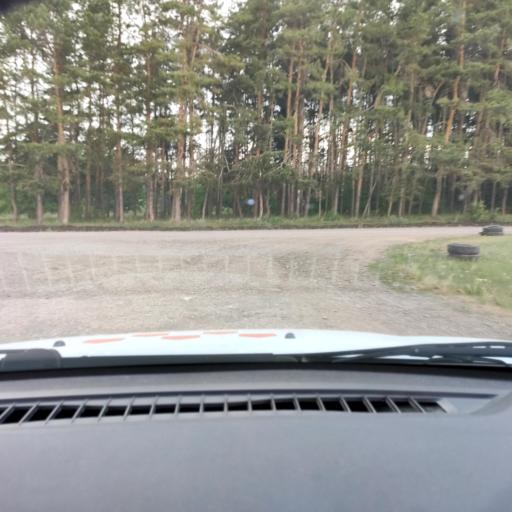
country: RU
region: Bashkortostan
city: Chishmy
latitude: 54.6128
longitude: 55.3950
